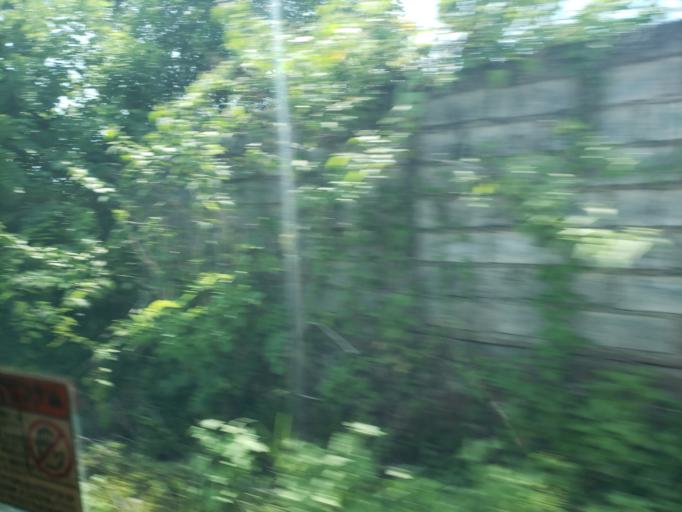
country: ID
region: Bali
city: Kangin
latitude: -8.8359
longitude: 115.1519
